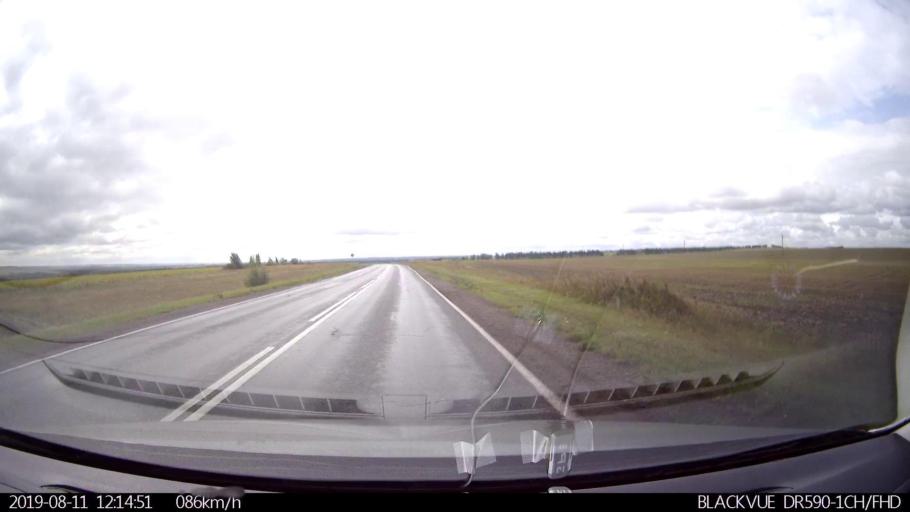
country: RU
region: Ulyanovsk
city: Ignatovka
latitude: 53.9480
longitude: 47.9744
